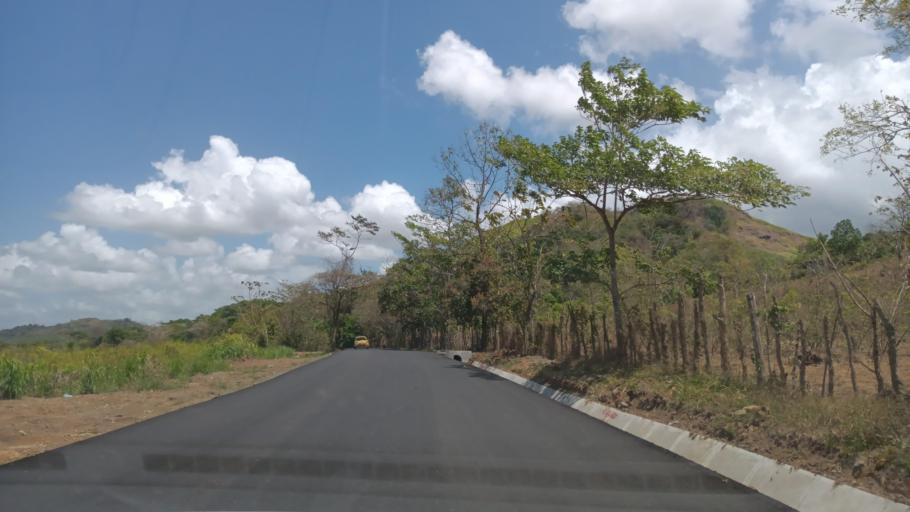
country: PA
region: Panama
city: Alcalde Diaz
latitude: 9.0882
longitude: -79.5778
